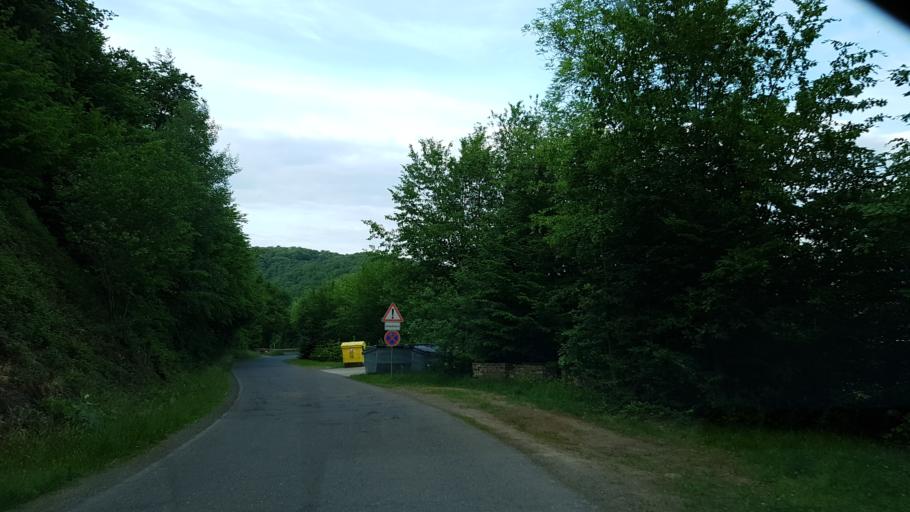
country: DE
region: North Rhine-Westphalia
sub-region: Regierungsbezirk Koln
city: Eitorf
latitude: 50.7772
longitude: 7.4153
